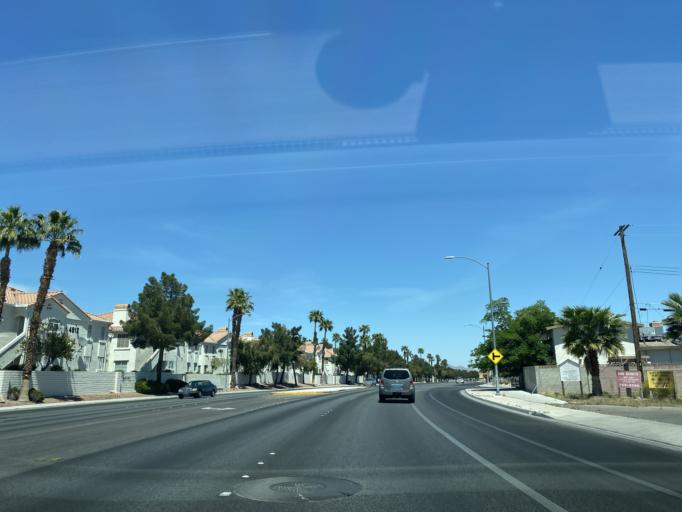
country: US
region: Nevada
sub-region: Clark County
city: Las Vegas
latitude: 36.1967
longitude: -115.2029
